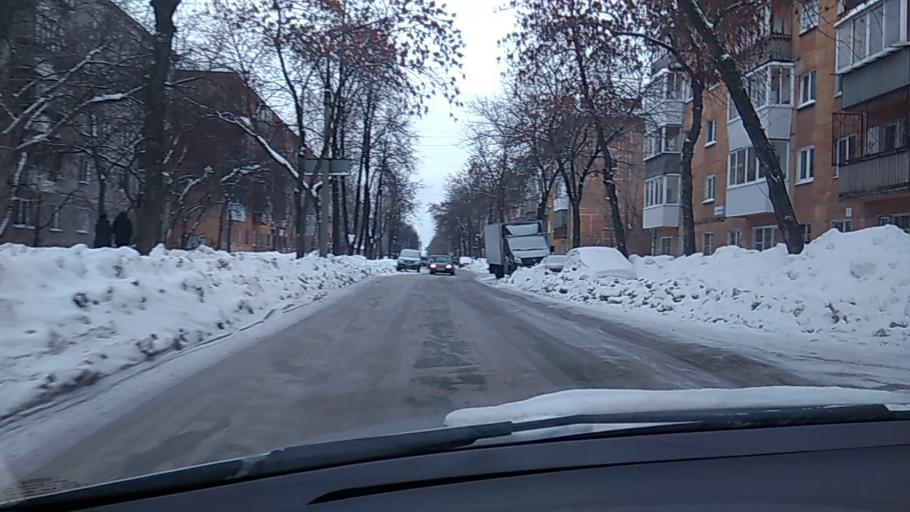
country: RU
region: Sverdlovsk
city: Yekaterinburg
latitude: 56.8903
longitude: 60.5706
